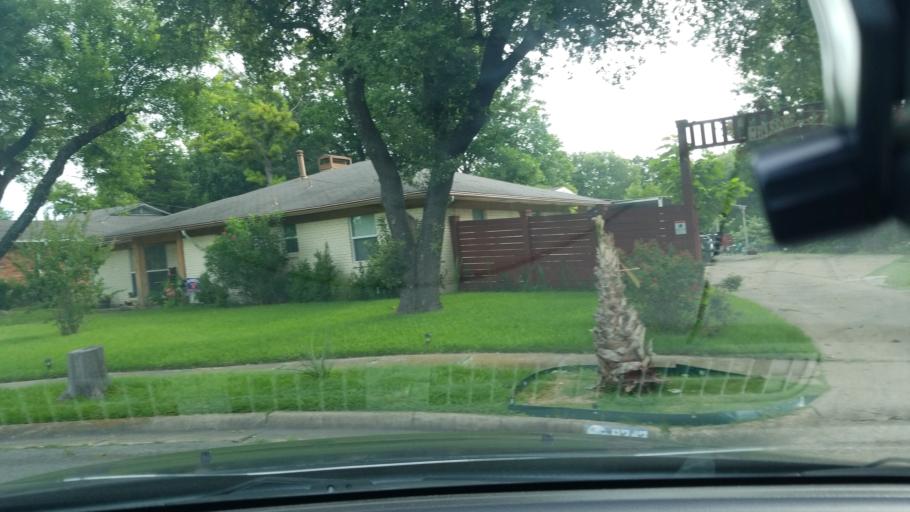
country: US
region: Texas
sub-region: Dallas County
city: Balch Springs
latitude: 32.7532
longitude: -96.6633
